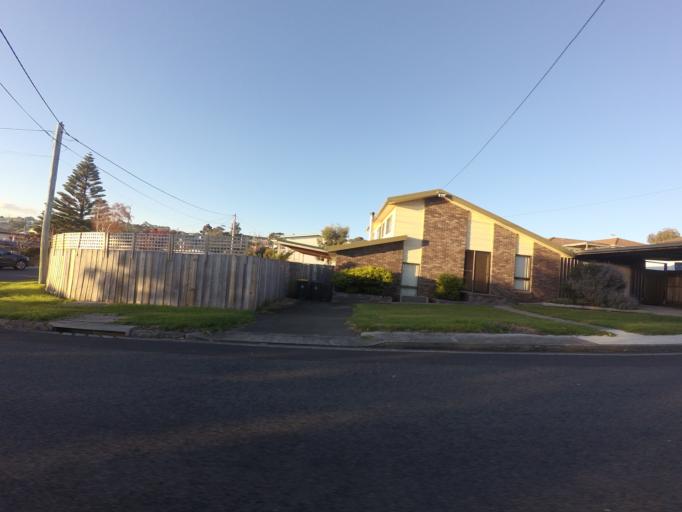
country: AU
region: Tasmania
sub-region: Sorell
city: Sorell
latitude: -42.8019
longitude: 147.5266
